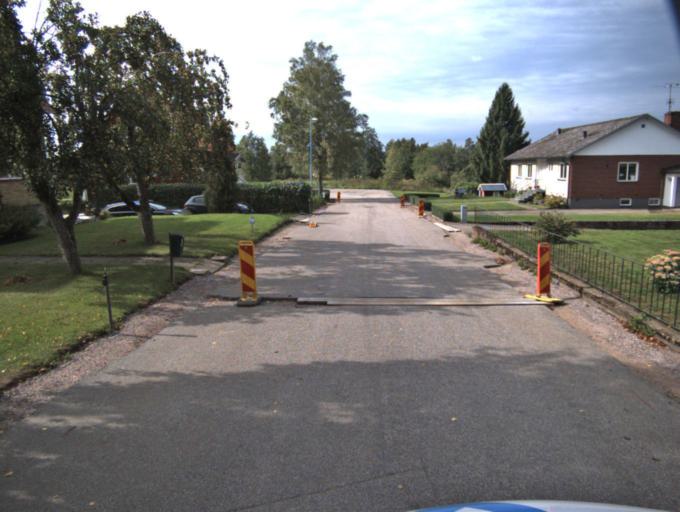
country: SE
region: Vaestra Goetaland
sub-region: Falkopings Kommun
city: Falkoeping
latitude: 57.9825
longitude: 13.5344
